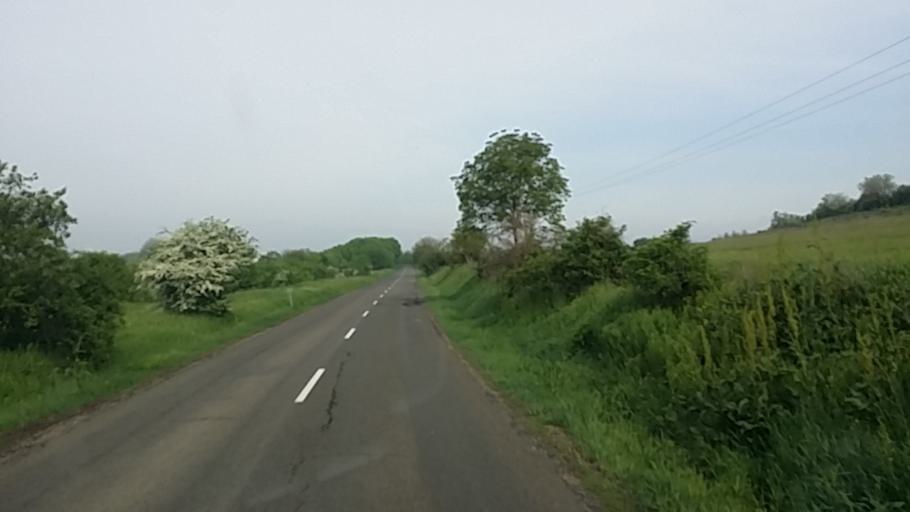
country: HU
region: Komarom-Esztergom
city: Esztergom
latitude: 47.7593
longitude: 18.7667
